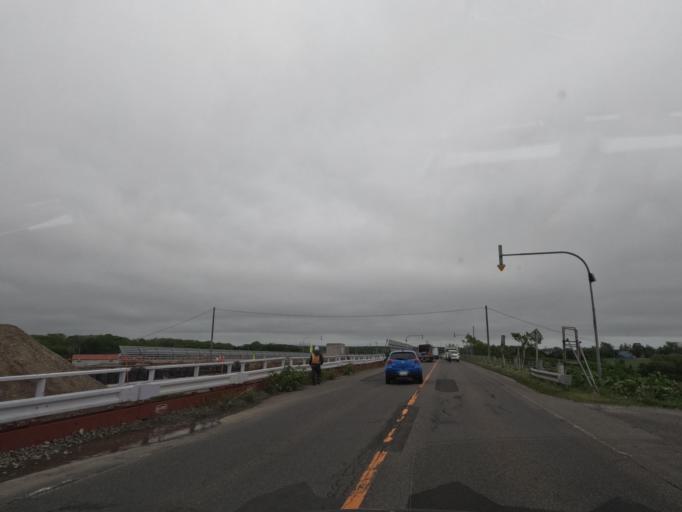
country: JP
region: Hokkaido
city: Ebetsu
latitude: 43.1393
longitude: 141.5138
